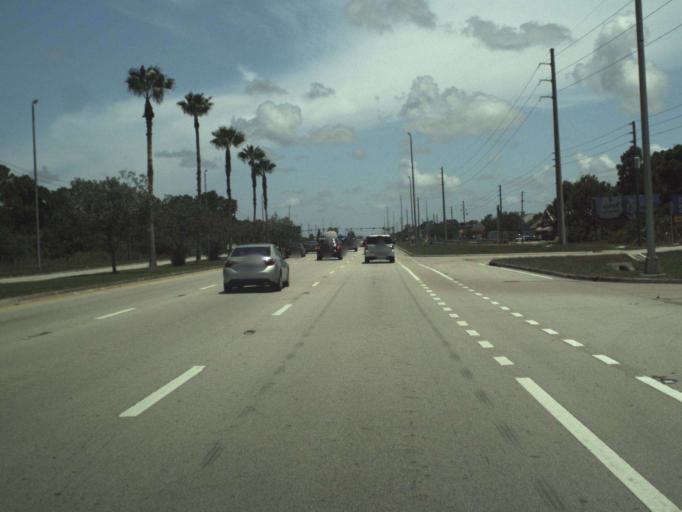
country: US
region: Florida
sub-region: Saint Lucie County
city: River Park
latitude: 27.3146
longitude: -80.3139
